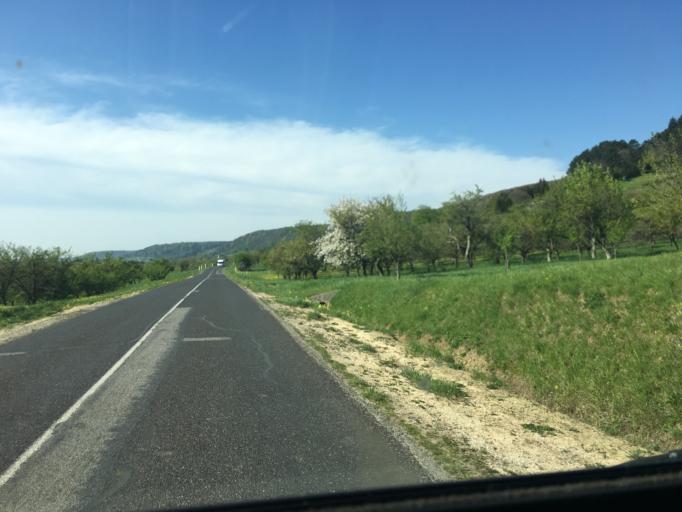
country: FR
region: Lorraine
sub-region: Departement de la Meuse
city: Vigneulles-les-Hattonchatel
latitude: 48.9197
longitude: 5.6803
